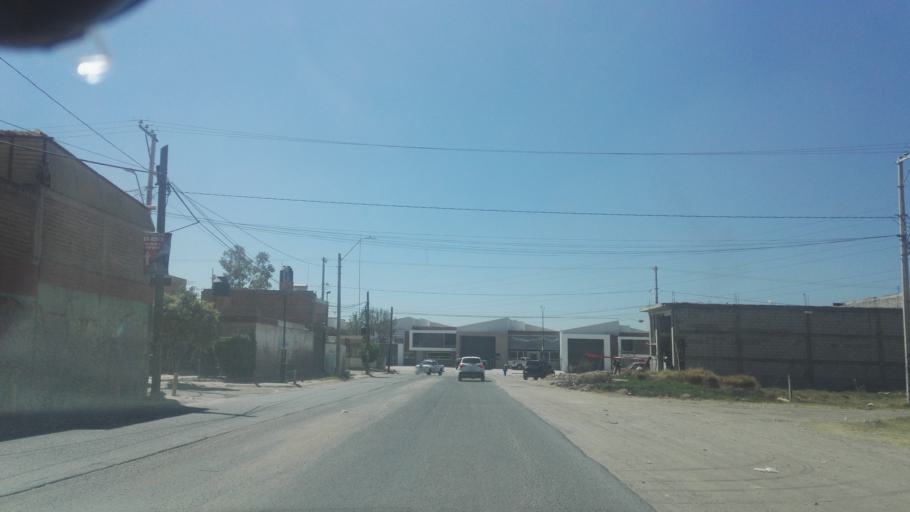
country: MX
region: Guanajuato
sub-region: Leon
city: Fraccionamiento Paraiso Real
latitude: 21.0905
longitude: -101.5939
